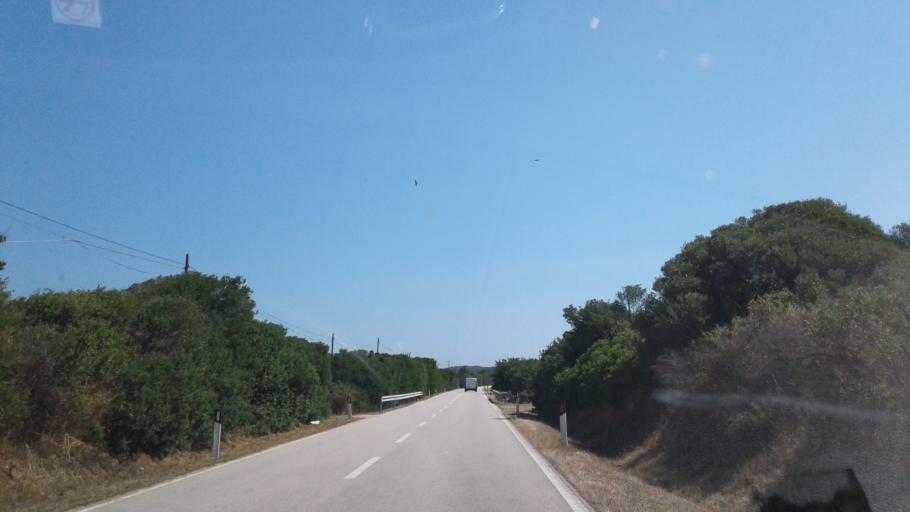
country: IT
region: Sardinia
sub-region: Provincia di Olbia-Tempio
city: Luogosanto
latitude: 41.1226
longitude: 9.2725
